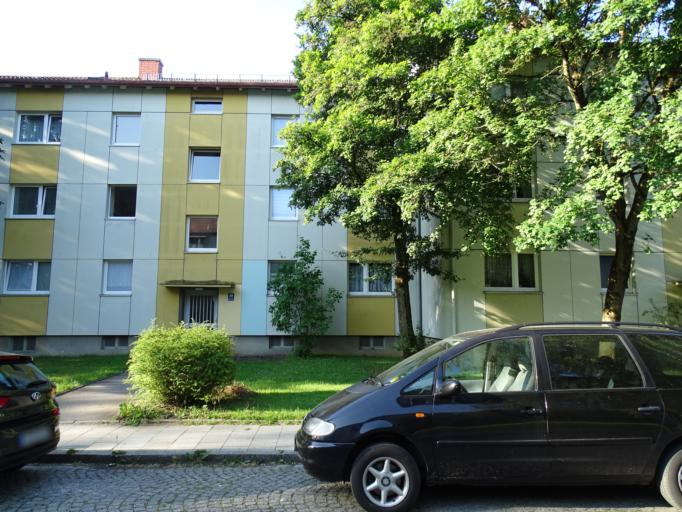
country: DE
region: Bavaria
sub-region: Upper Bavaria
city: Oberschleissheim
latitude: 48.2064
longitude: 11.5736
